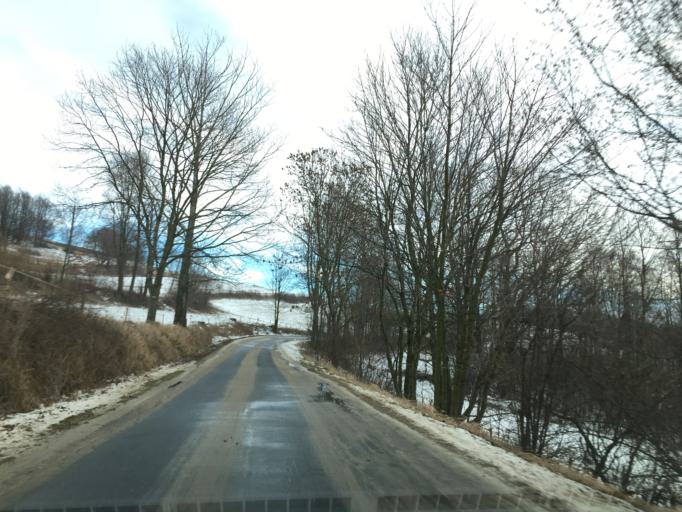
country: PL
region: Lower Silesian Voivodeship
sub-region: Powiat walbrzyski
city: Jedlina-Zdroj
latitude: 50.7374
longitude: 16.3722
